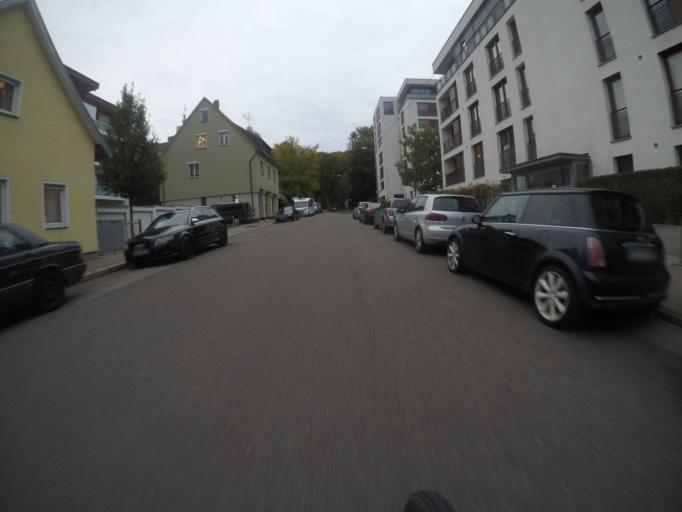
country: DE
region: Baden-Wuerttemberg
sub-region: Regierungsbezirk Stuttgart
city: Stuttgart-Ost
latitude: 48.7951
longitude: 9.2089
